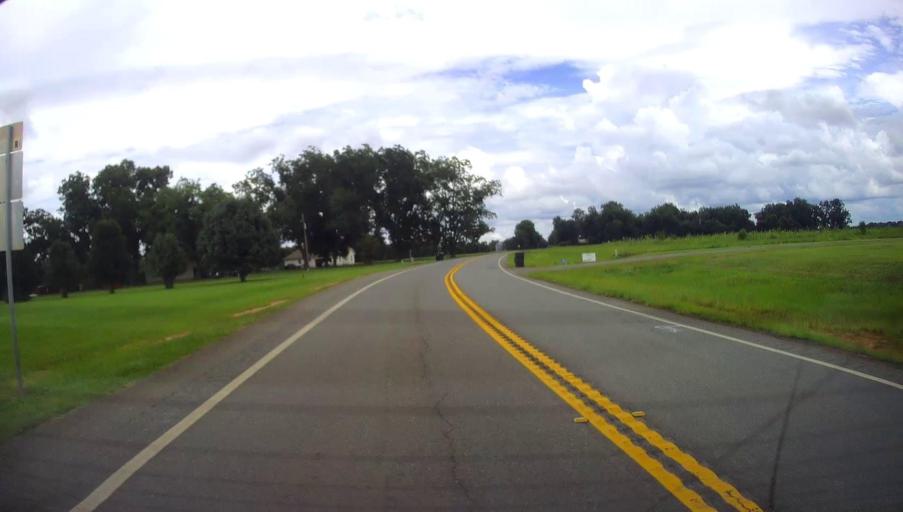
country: US
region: Georgia
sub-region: Schley County
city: Ellaville
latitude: 32.2247
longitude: -84.2842
